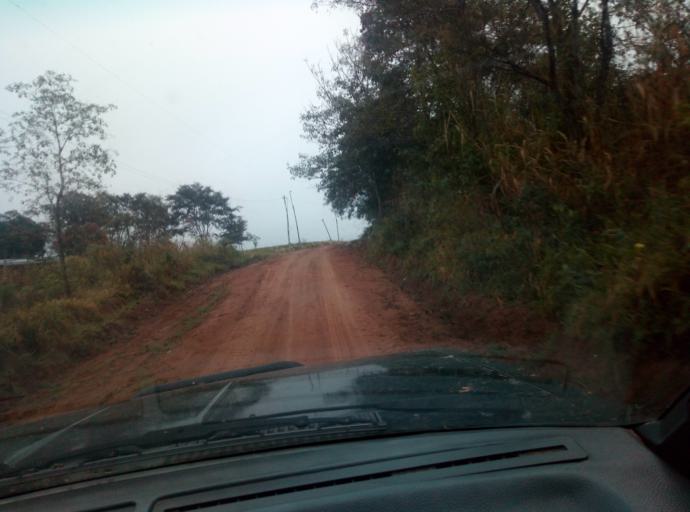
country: PY
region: Caaguazu
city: Carayao
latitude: -25.1904
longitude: -56.3196
